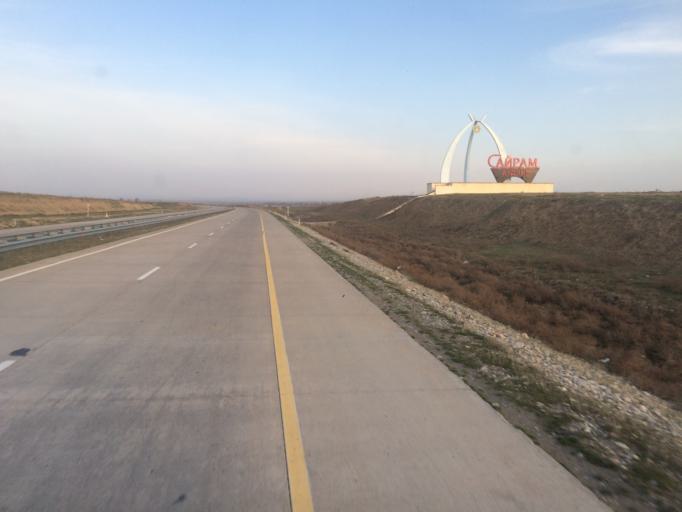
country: KZ
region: Ongtustik Qazaqstan
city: Shymkent
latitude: 42.4933
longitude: 69.4768
